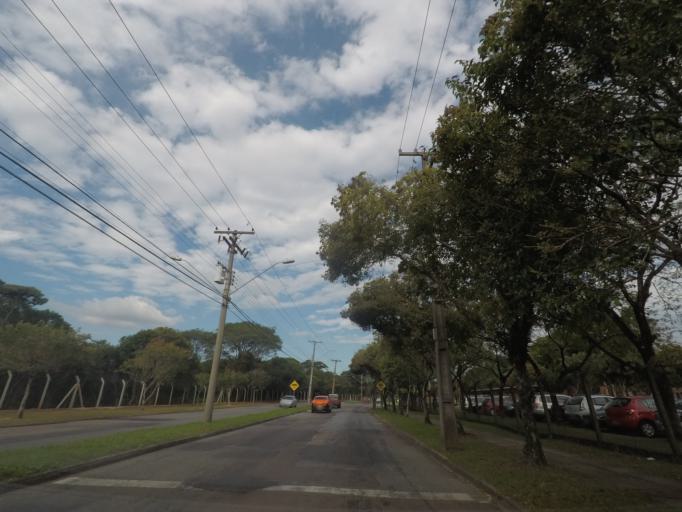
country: BR
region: Parana
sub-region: Sao Jose Dos Pinhais
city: Sao Jose dos Pinhais
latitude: -25.5317
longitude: -49.3094
